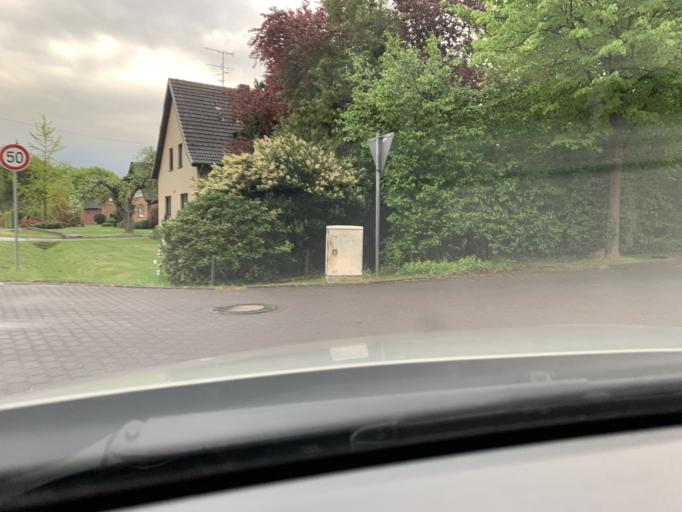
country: DE
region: North Rhine-Westphalia
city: Rietberg
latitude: 51.8017
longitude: 8.3852
